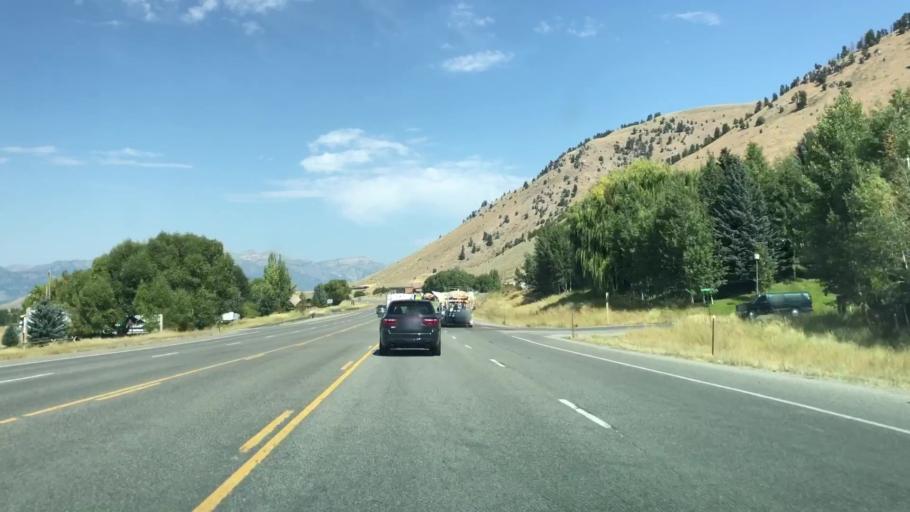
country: US
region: Wyoming
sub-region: Teton County
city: South Park
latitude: 43.4254
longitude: -110.7778
